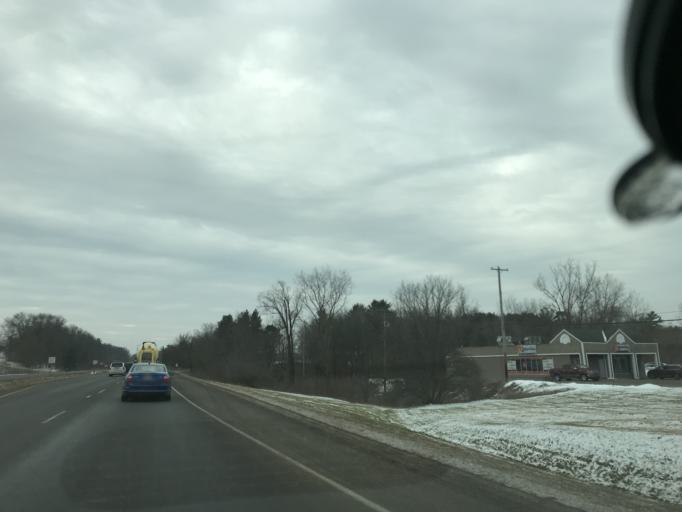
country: US
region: Michigan
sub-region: Kent County
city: Rockford
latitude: 43.1170
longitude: -85.5487
